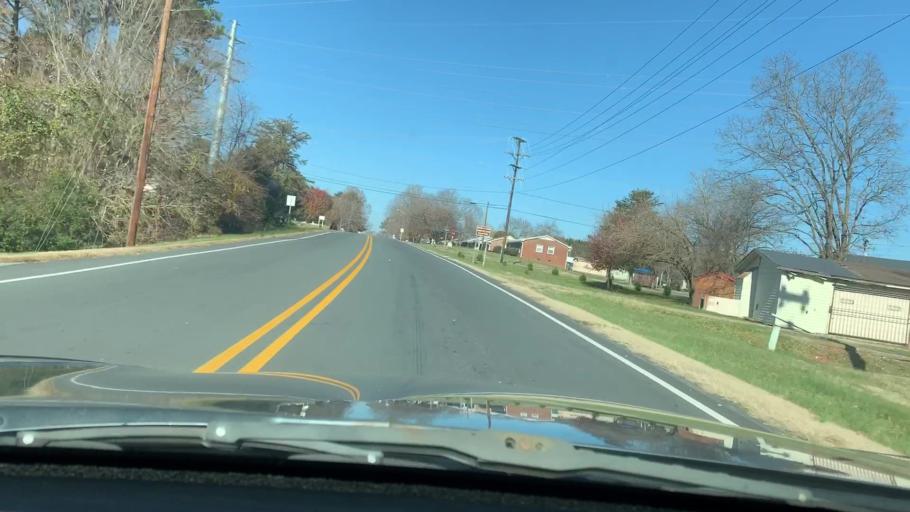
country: US
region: North Carolina
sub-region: Alamance County
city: Haw River
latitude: 36.0971
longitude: -79.3495
